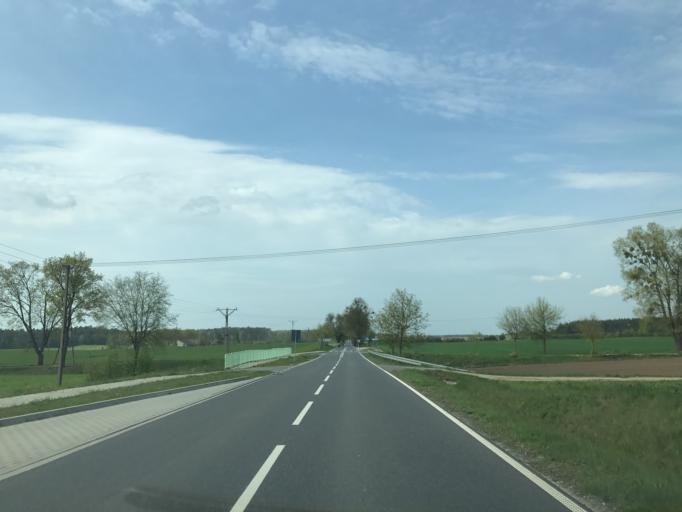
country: PL
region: Warmian-Masurian Voivodeship
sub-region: Powiat dzialdowski
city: Lidzbark
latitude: 53.3682
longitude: 19.8177
